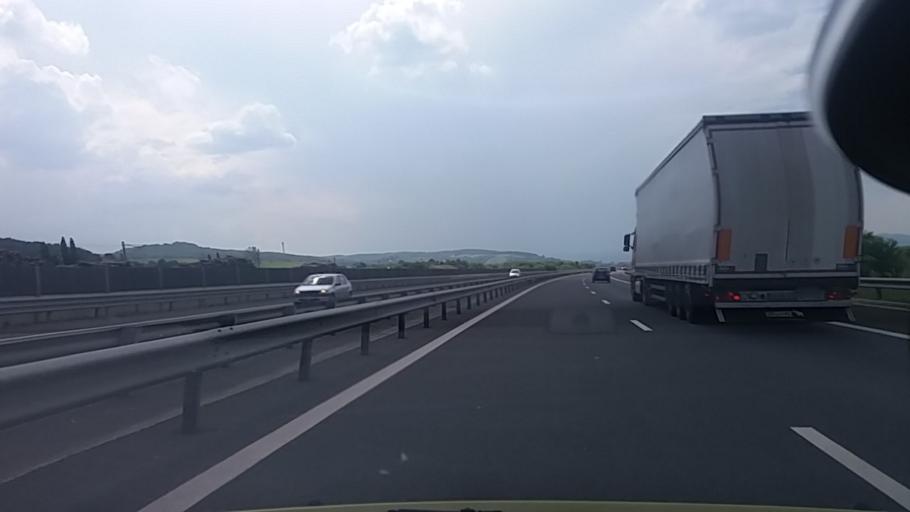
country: RO
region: Hunedoara
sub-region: Comuna Turdas
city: Turdas
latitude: 45.8369
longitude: 23.1078
